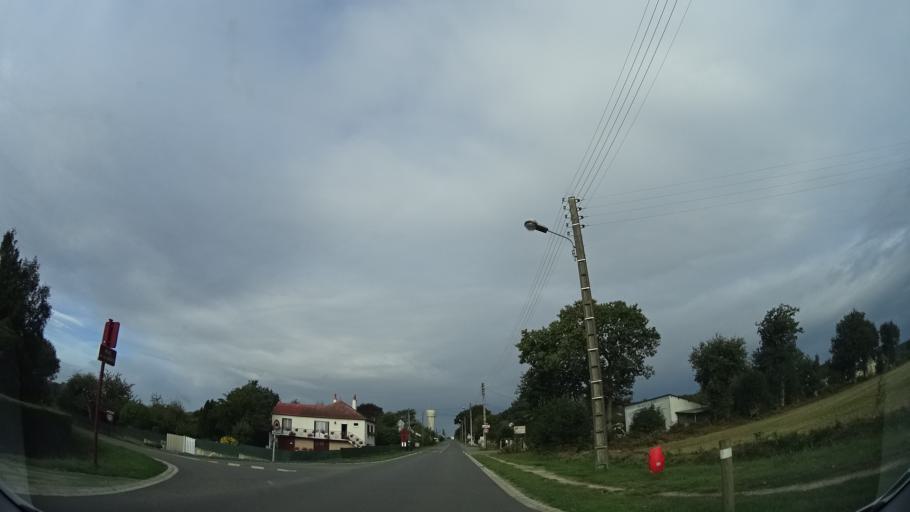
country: FR
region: Brittany
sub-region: Departement d'Ille-et-Vilaine
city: Guipel
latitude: 48.2985
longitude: -1.7311
